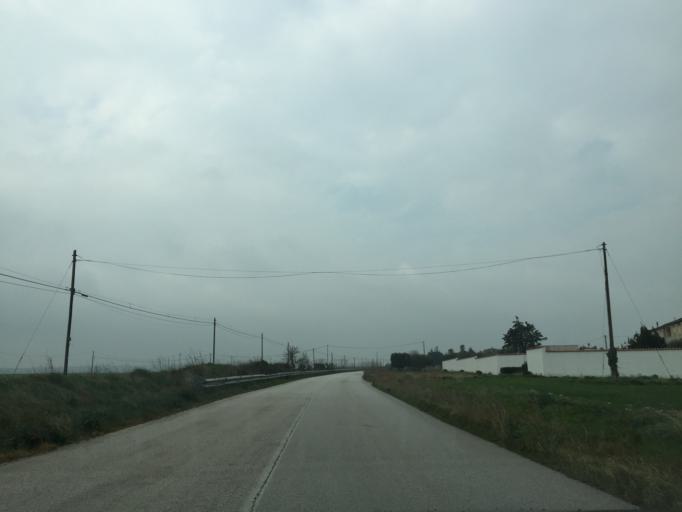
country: IT
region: Apulia
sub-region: Provincia di Foggia
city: Castelluccio dei Sauri
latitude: 41.3962
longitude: 15.4206
